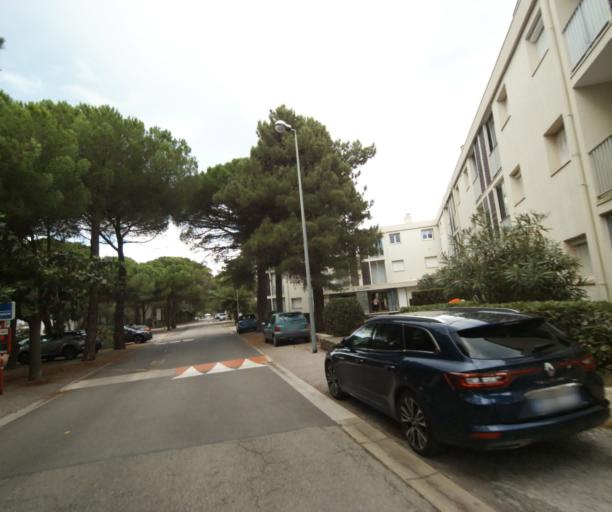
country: FR
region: Languedoc-Roussillon
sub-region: Departement des Pyrenees-Orientales
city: Argelers
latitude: 42.5625
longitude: 3.0452
